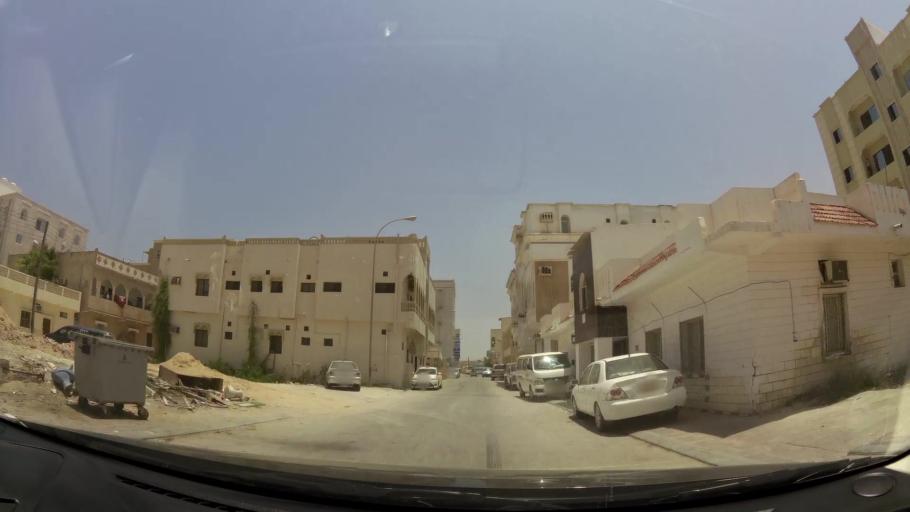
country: OM
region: Zufar
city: Salalah
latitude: 17.0172
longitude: 54.1081
